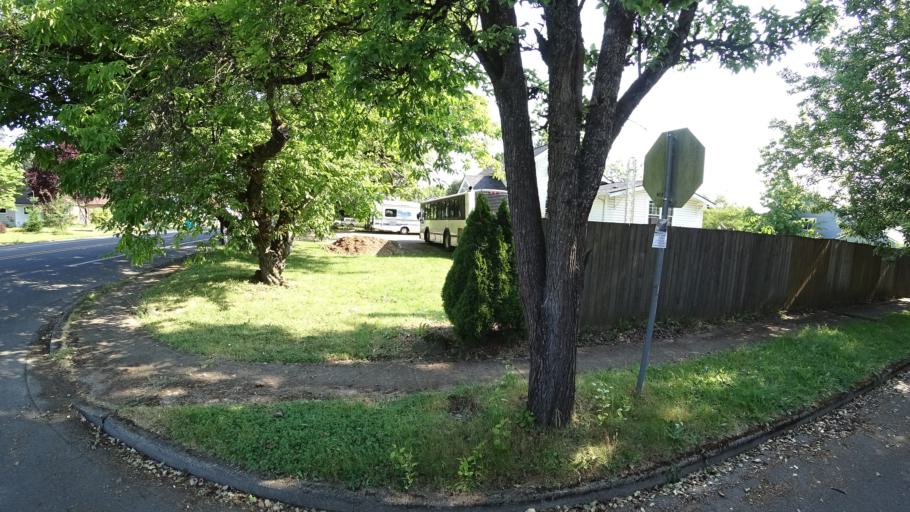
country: US
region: Oregon
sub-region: Clackamas County
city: Oatfield
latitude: 45.4424
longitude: -122.5991
